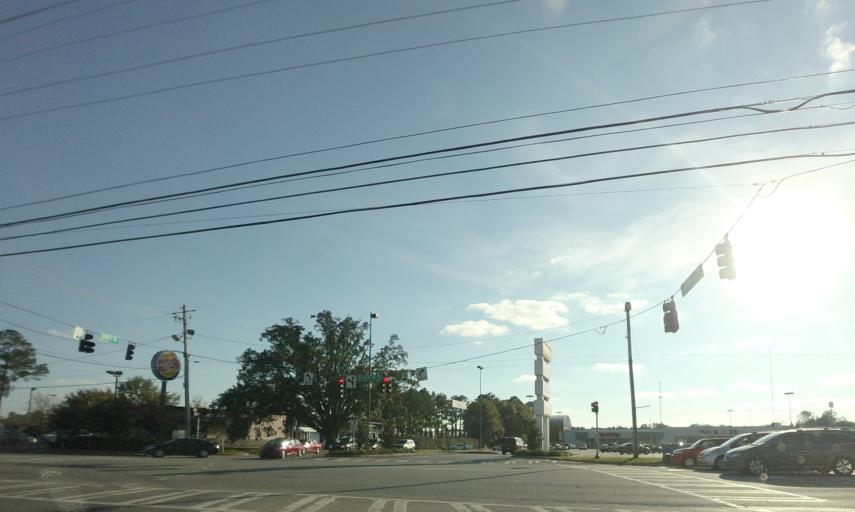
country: US
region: Georgia
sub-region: Lowndes County
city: Remerton
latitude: 30.8421
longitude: -83.3247
